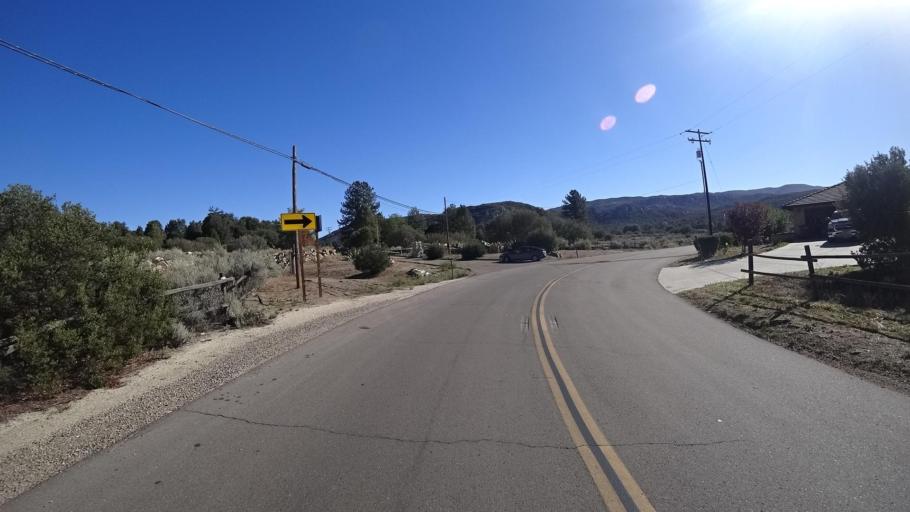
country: US
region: California
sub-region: San Diego County
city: Pine Valley
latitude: 32.8384
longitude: -116.5343
